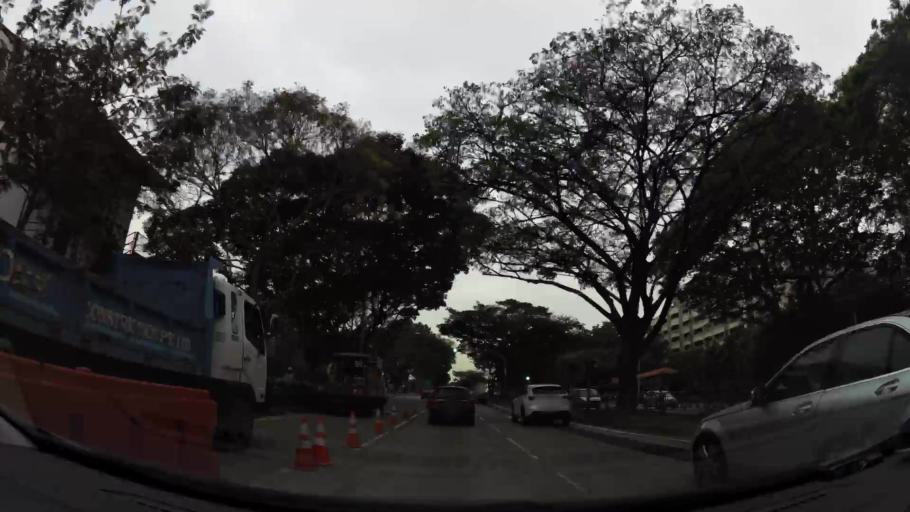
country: SG
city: Singapore
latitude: 1.3727
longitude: 103.8769
